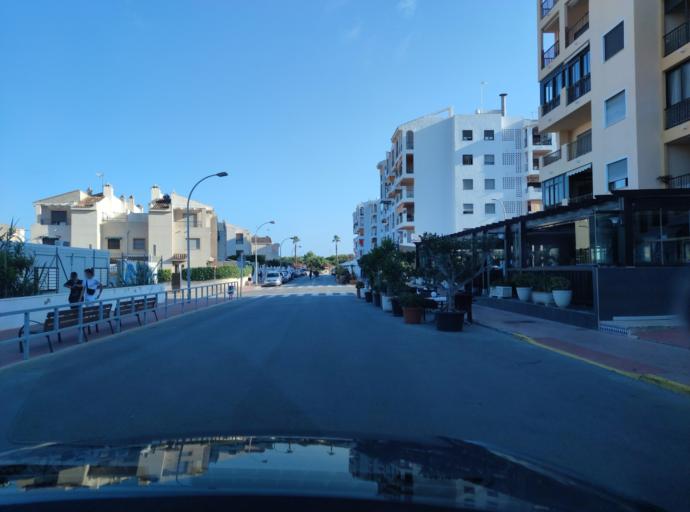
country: ES
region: Valencia
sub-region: Provincia de Alicante
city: Guardamar del Segura
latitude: 38.0815
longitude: -0.6516
